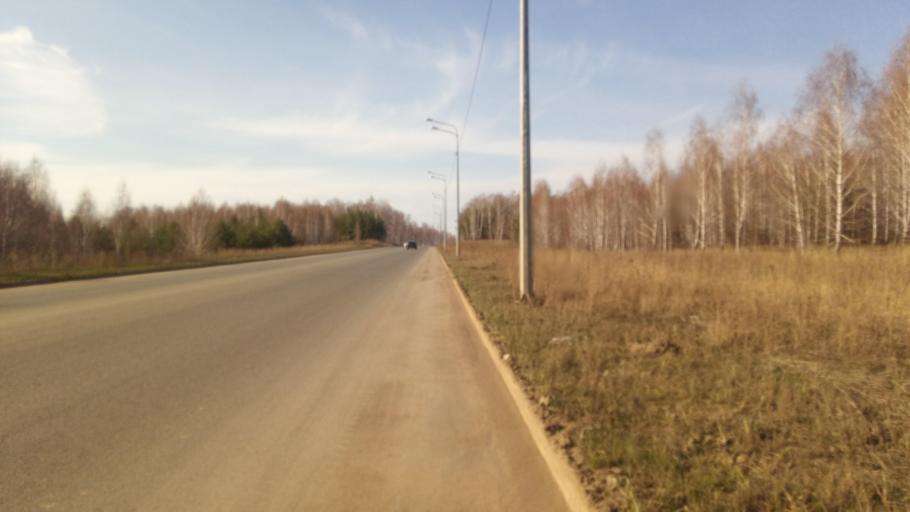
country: RU
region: Chelyabinsk
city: Sargazy
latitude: 55.1170
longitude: 61.2539
